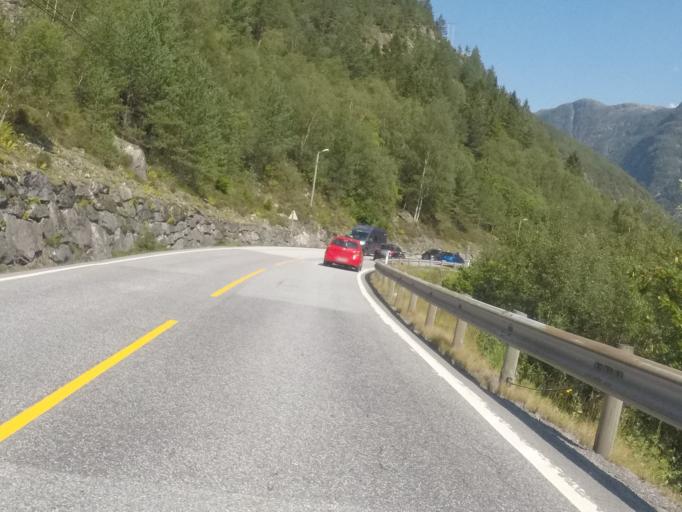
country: NO
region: Sogn og Fjordane
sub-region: Gaular
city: Sande
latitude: 61.2059
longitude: 5.8112
